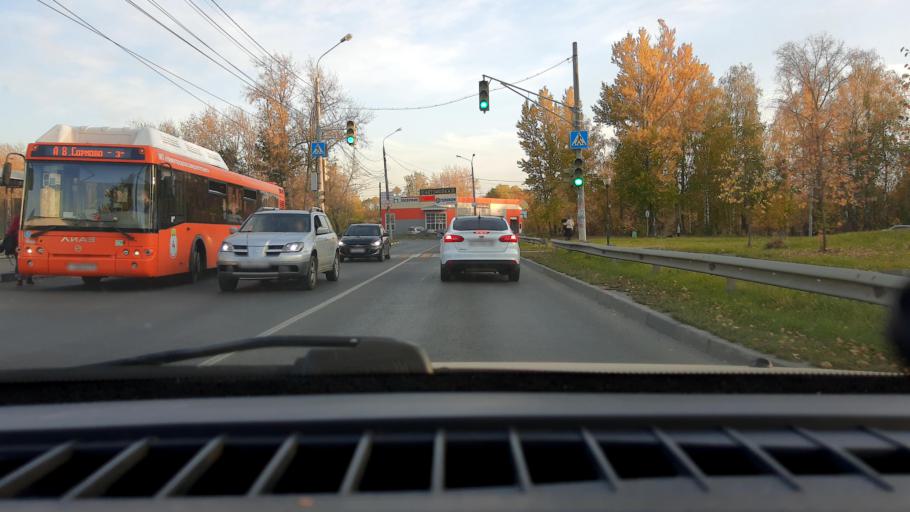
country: RU
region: Nizjnij Novgorod
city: Gorbatovka
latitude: 56.3438
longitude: 43.8077
